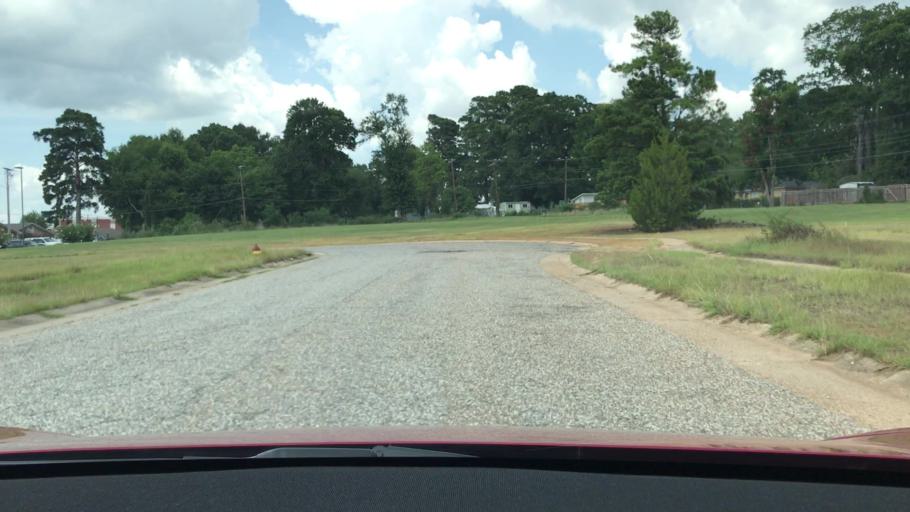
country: US
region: Louisiana
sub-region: De Soto Parish
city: Stonewall
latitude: 32.3972
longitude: -93.8043
